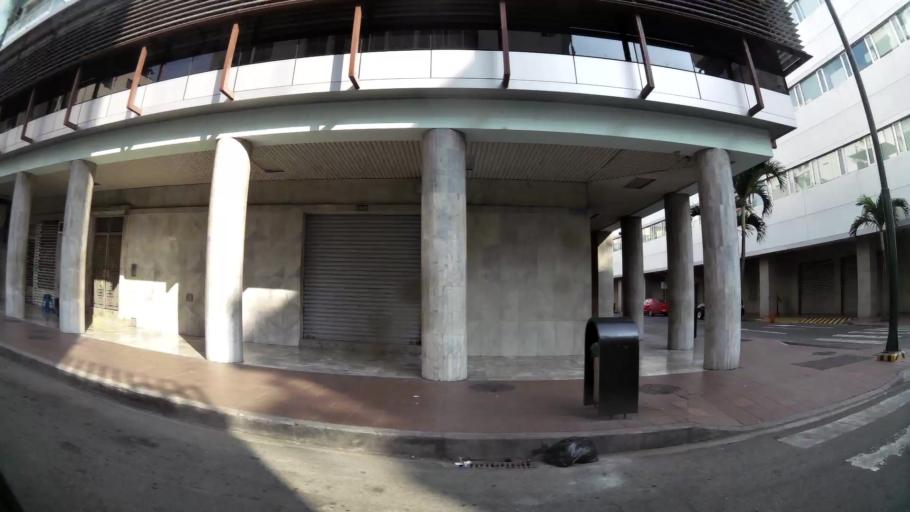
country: EC
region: Guayas
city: Guayaquil
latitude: -2.1926
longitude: -79.8838
